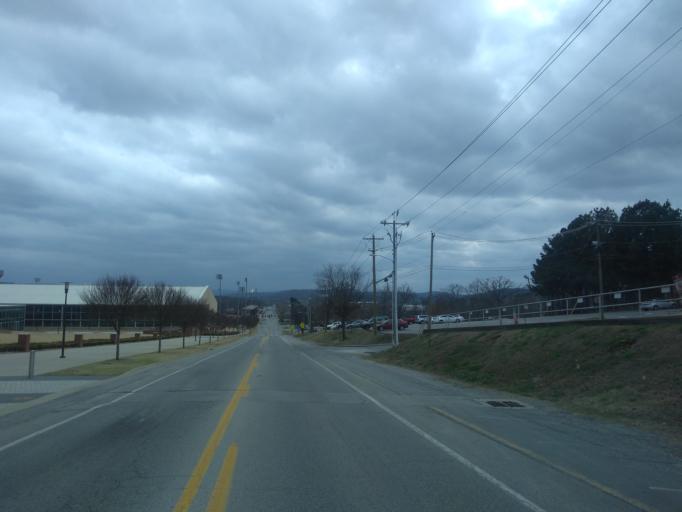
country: US
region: Arkansas
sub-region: Washington County
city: Fayetteville
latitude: 36.0672
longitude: -94.1801
